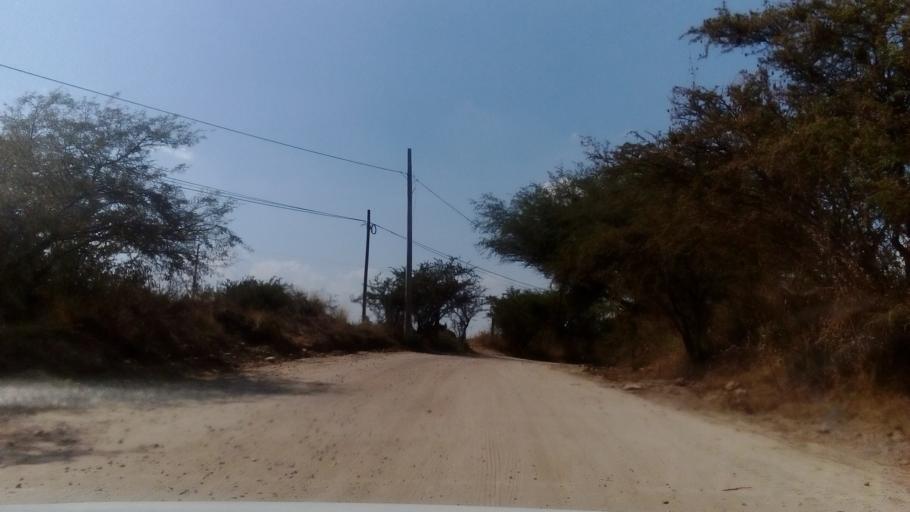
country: MX
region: Guanajuato
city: Duarte
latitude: 21.0823
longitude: -101.5076
